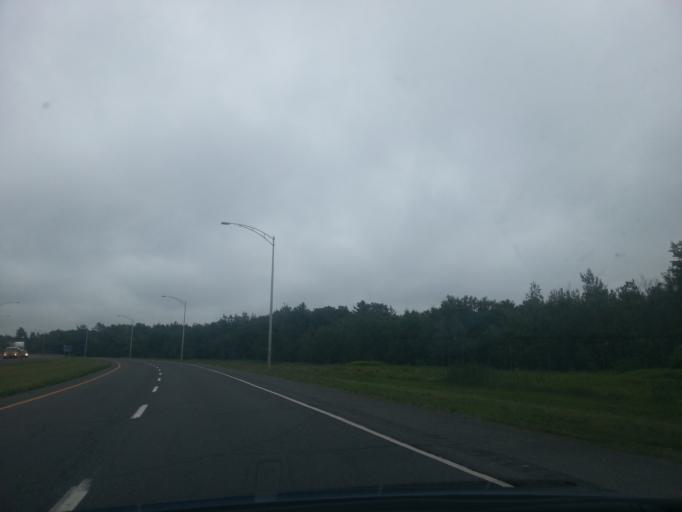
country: CA
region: Quebec
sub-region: Centre-du-Quebec
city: Drummondville
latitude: 45.9093
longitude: -72.4944
